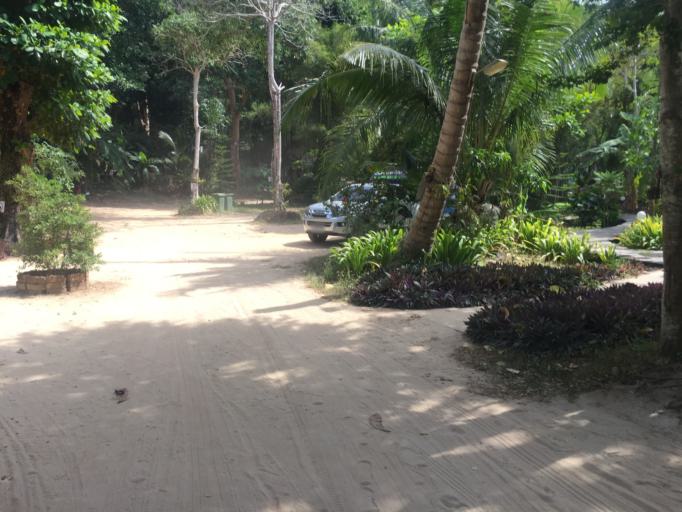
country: TH
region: Trat
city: Laem Ngop
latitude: 12.1166
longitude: 102.2657
